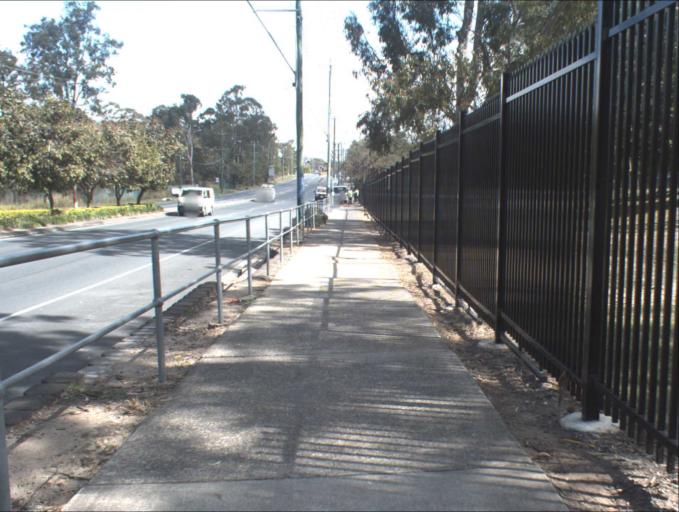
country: AU
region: Queensland
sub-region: Logan
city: Waterford West
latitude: -27.6865
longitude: 153.1067
